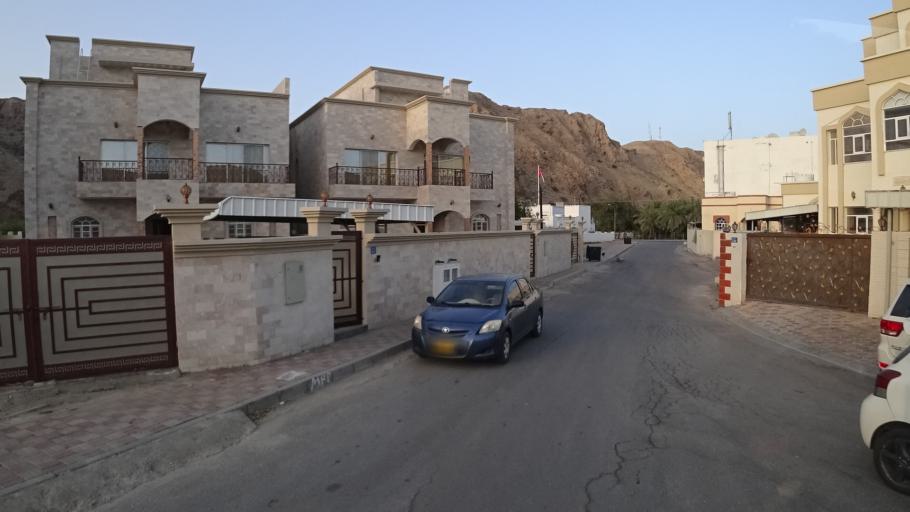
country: OM
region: Muhafazat Masqat
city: Muscat
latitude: 23.5081
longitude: 58.6612
